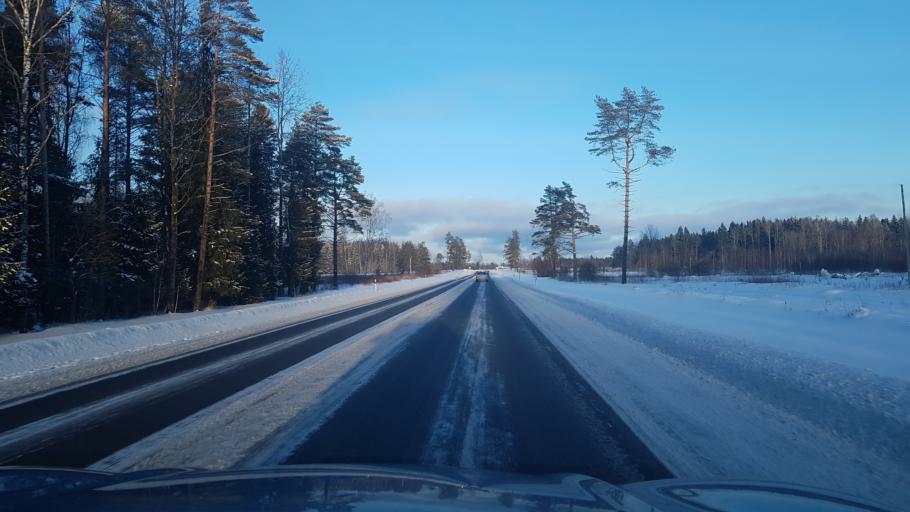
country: EE
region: Ida-Virumaa
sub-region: Toila vald
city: Voka
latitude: 59.3854
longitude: 27.5707
